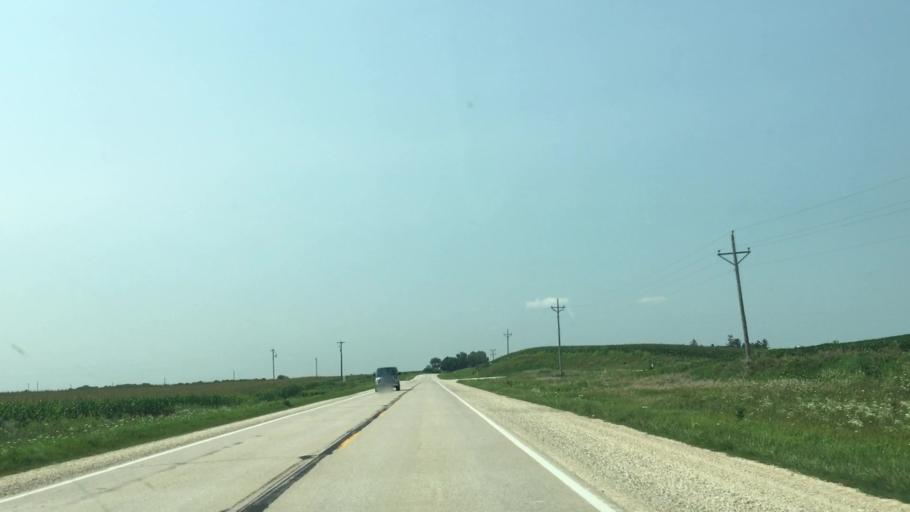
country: US
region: Iowa
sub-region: Fayette County
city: West Union
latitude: 43.0955
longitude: -91.8616
